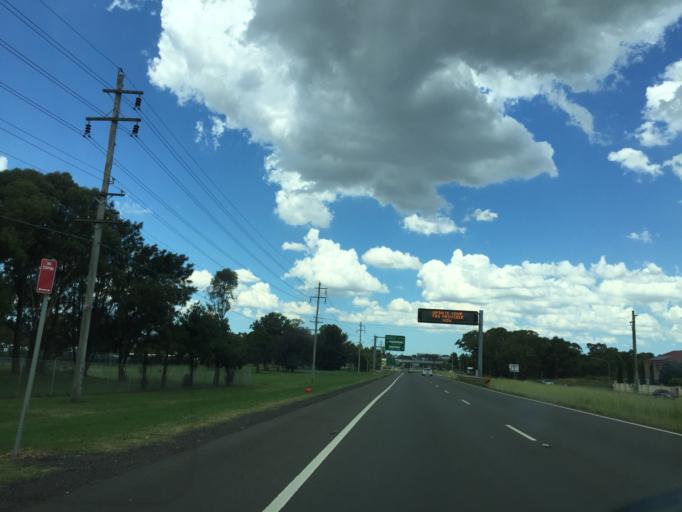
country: AU
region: New South Wales
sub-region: Blacktown
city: Doonside
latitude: -33.7877
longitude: 150.8501
